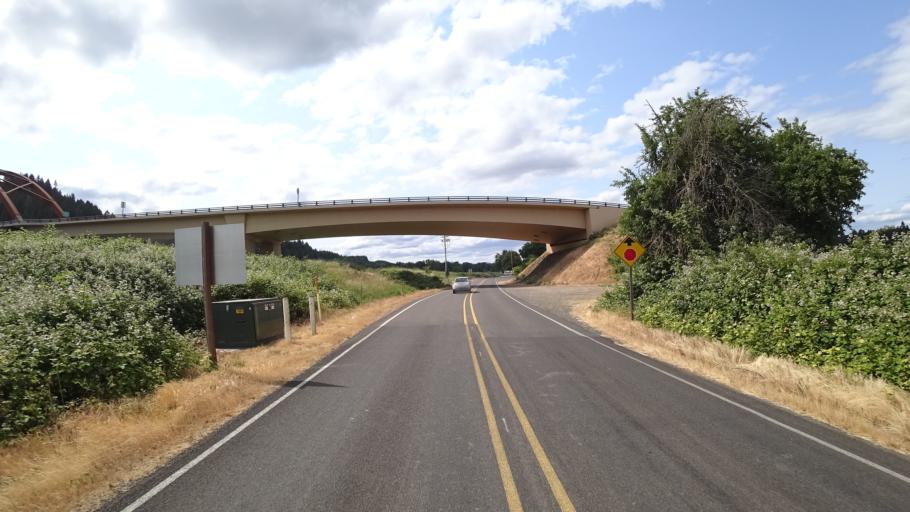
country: US
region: Oregon
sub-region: Washington County
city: Bethany
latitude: 45.6281
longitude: -122.8144
